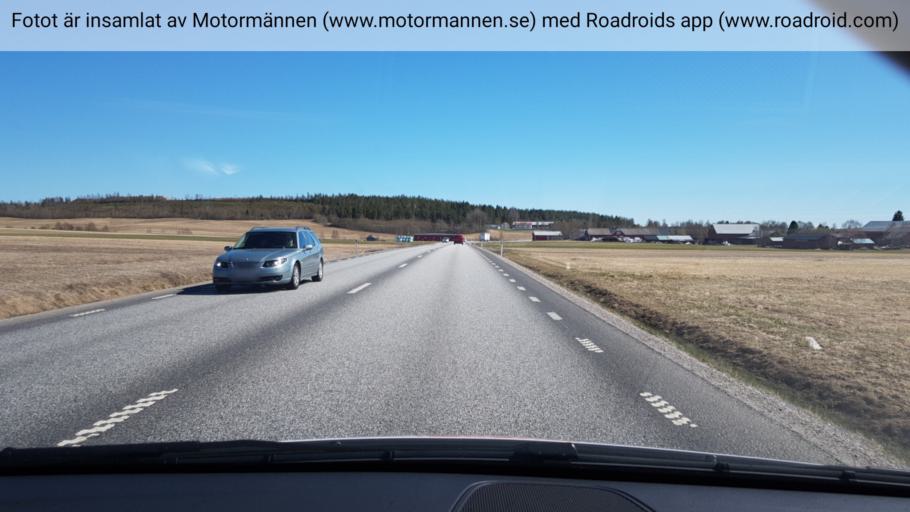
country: SE
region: Vaesterbotten
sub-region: Umea Kommun
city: Roback
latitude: 63.8690
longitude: 20.0774
